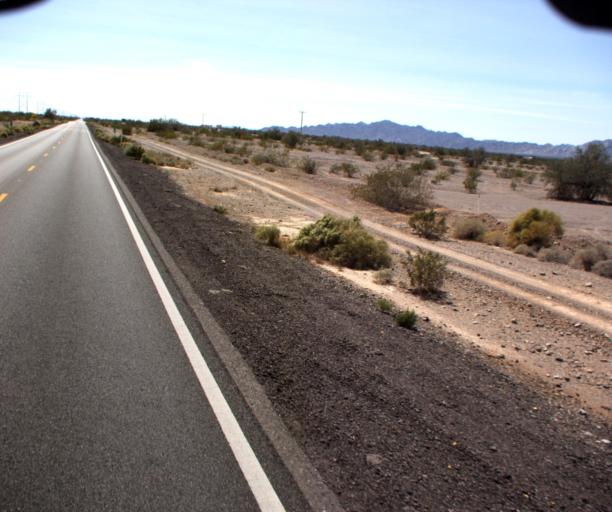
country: US
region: Arizona
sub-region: La Paz County
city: Quartzsite
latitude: 33.6312
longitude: -114.2171
